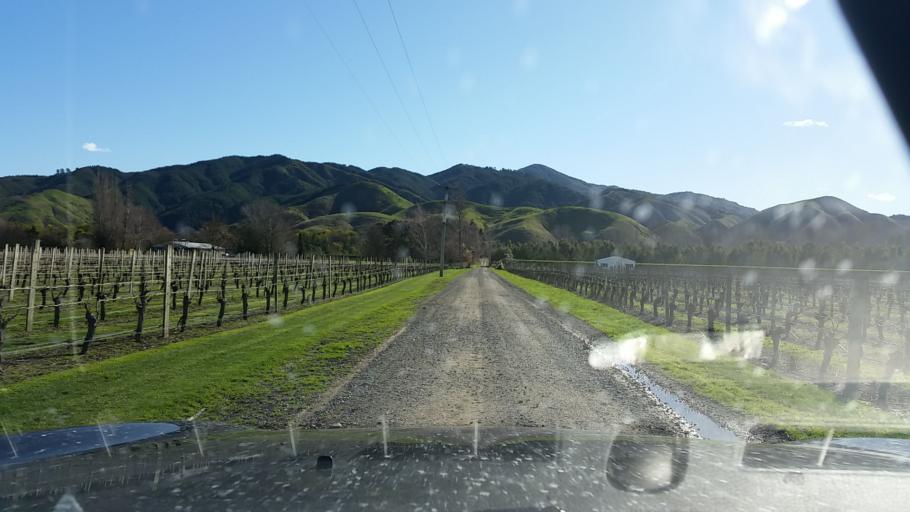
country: NZ
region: Marlborough
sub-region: Marlborough District
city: Blenheim
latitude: -41.4462
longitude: 173.9367
